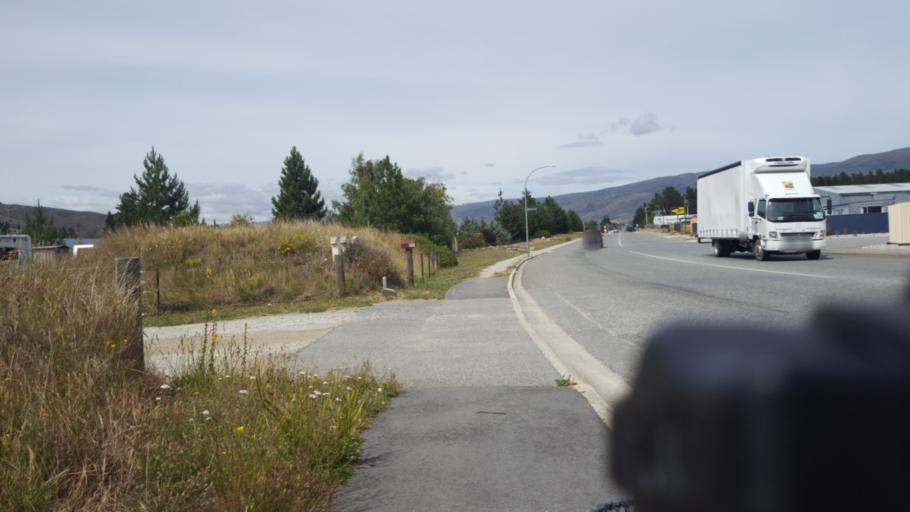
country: NZ
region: Otago
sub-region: Queenstown-Lakes District
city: Wanaka
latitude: -45.0528
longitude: 169.1956
